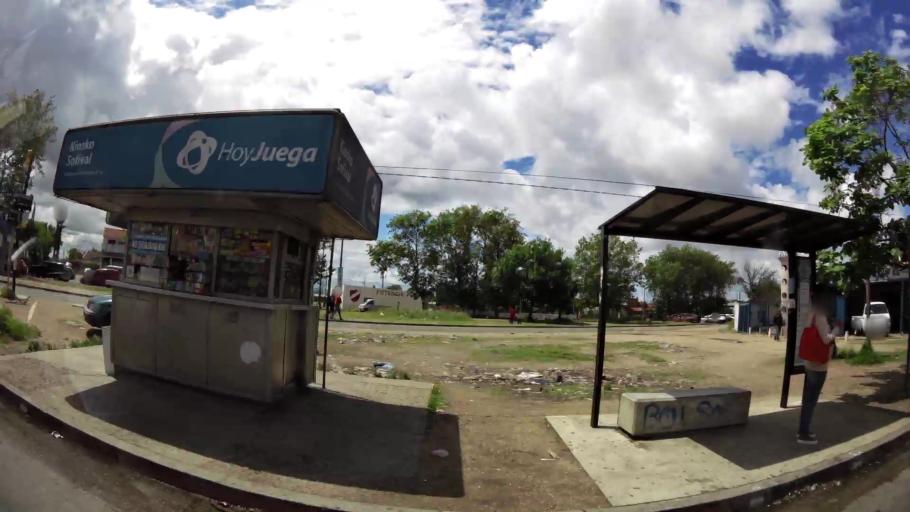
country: UY
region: Montevideo
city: Montevideo
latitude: -34.8293
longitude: -56.1413
